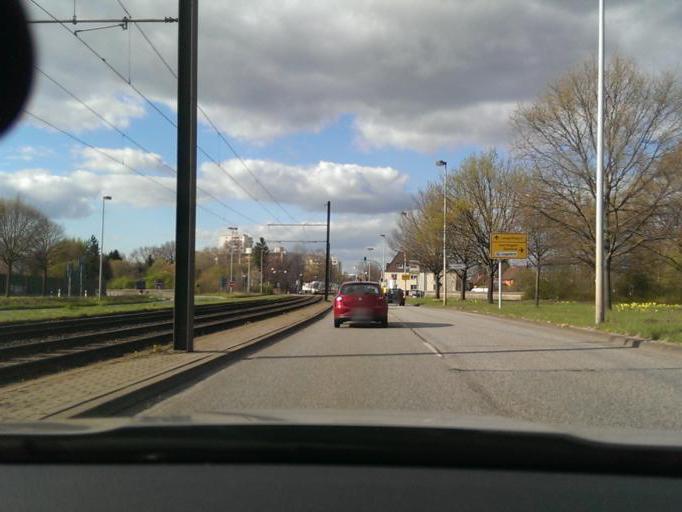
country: DE
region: Lower Saxony
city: Langenhagen
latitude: 52.4283
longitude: 9.7323
